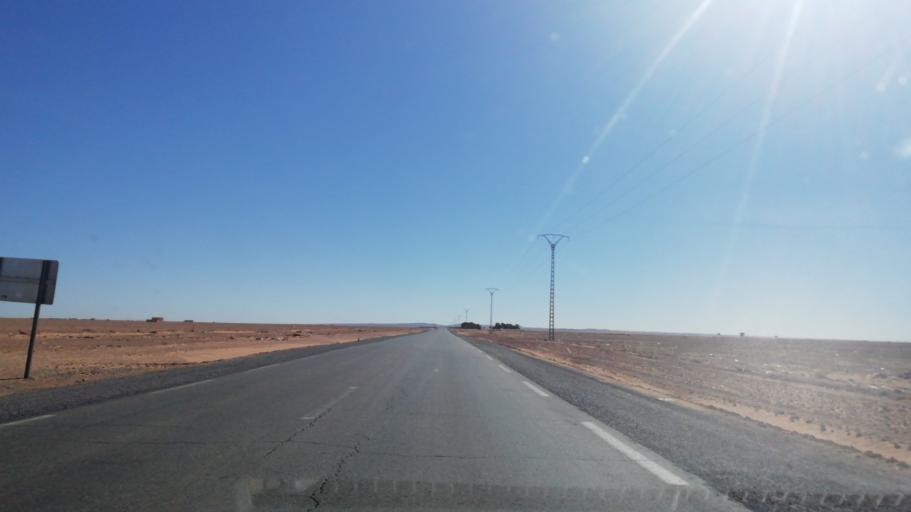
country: DZ
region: Saida
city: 'Ain el Hadjar
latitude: 34.0141
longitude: 0.1131
